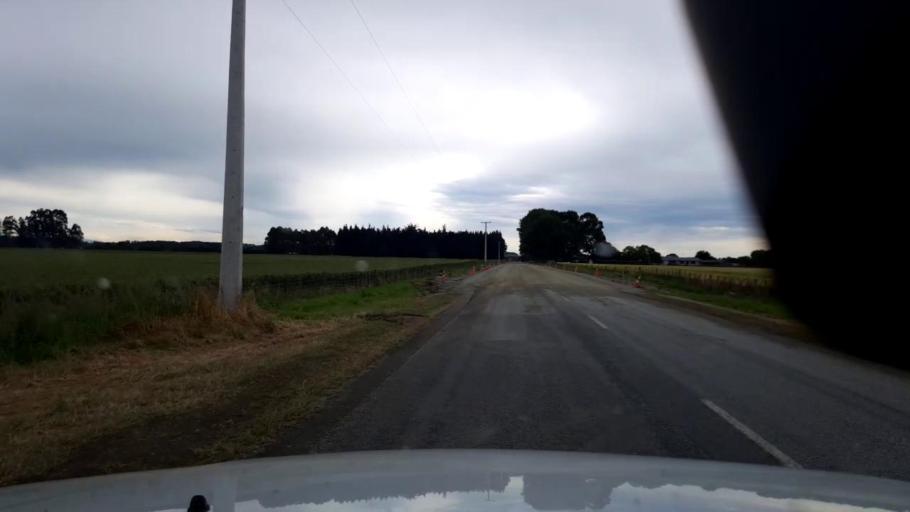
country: NZ
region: Canterbury
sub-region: Timaru District
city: Pleasant Point
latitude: -44.2795
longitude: 171.2470
